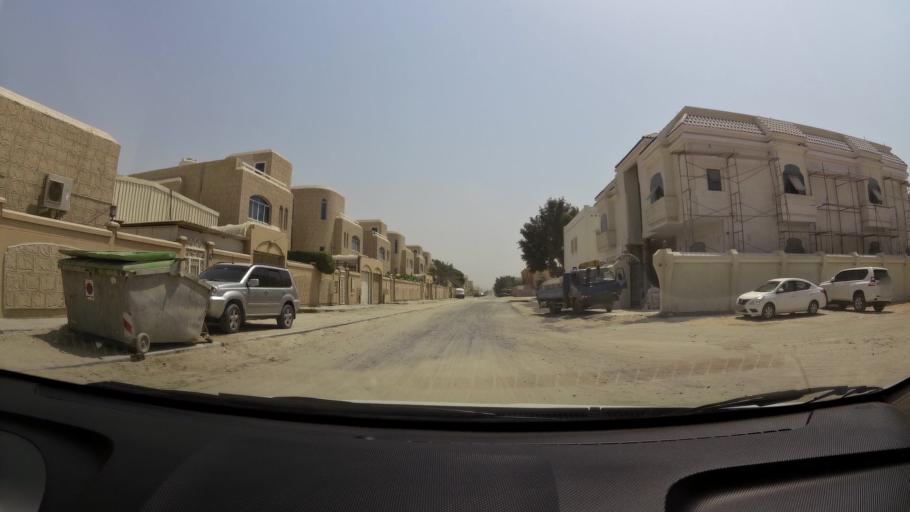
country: AE
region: Ajman
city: Ajman
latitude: 25.3942
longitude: 55.4266
